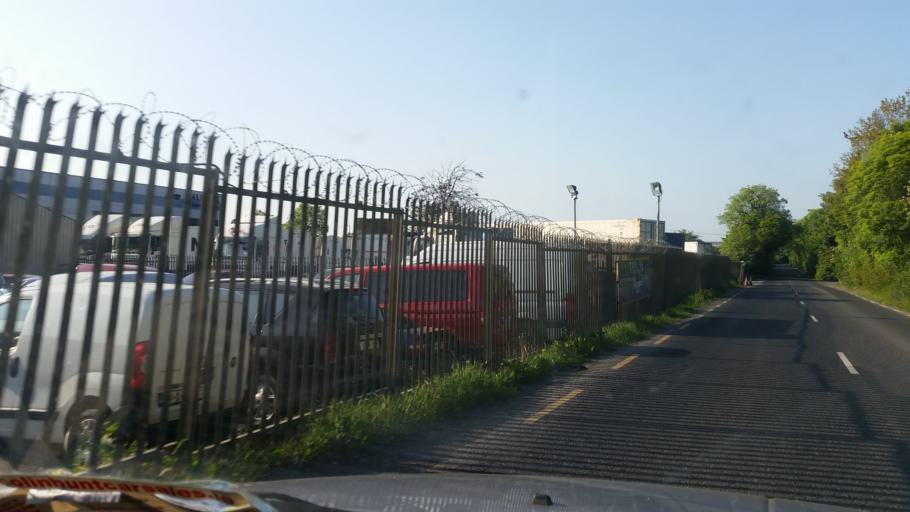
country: IE
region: Leinster
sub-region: Fingal County
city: Blanchardstown
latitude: 53.4149
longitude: -6.3439
